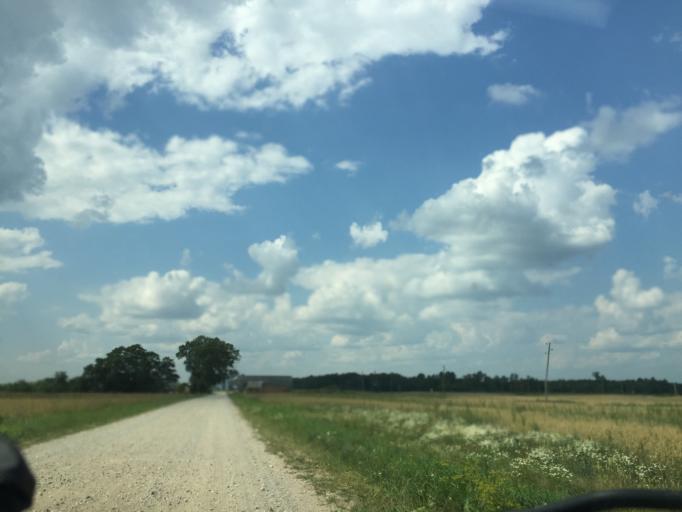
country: LT
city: Zagare
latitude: 56.3336
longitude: 23.0833
